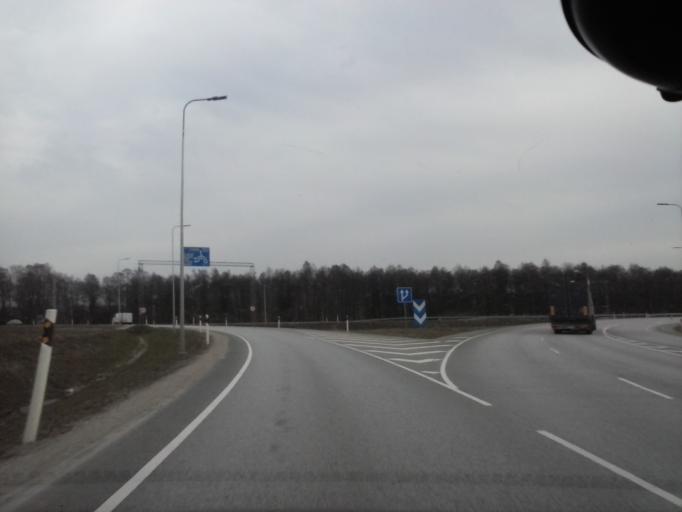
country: EE
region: Harju
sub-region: Rae vald
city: Jueri
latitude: 59.3532
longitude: 24.8791
